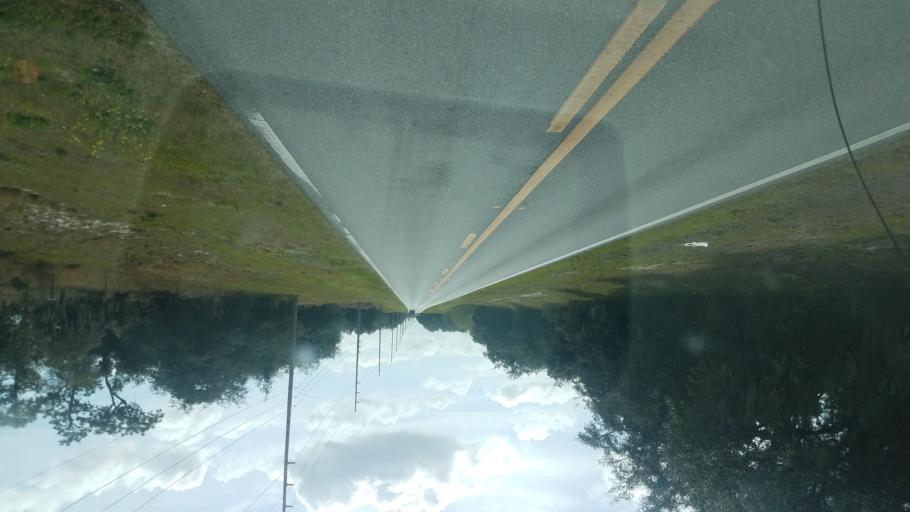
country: US
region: Florida
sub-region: Polk County
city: Lake Wales
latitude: 27.9486
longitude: -81.5378
